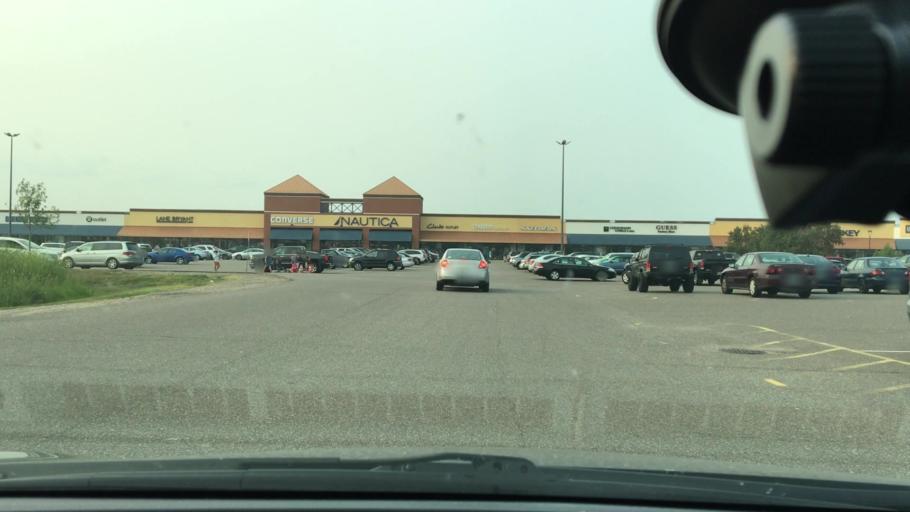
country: US
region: Minnesota
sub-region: Wright County
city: Albertville
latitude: 45.2452
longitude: -93.6680
